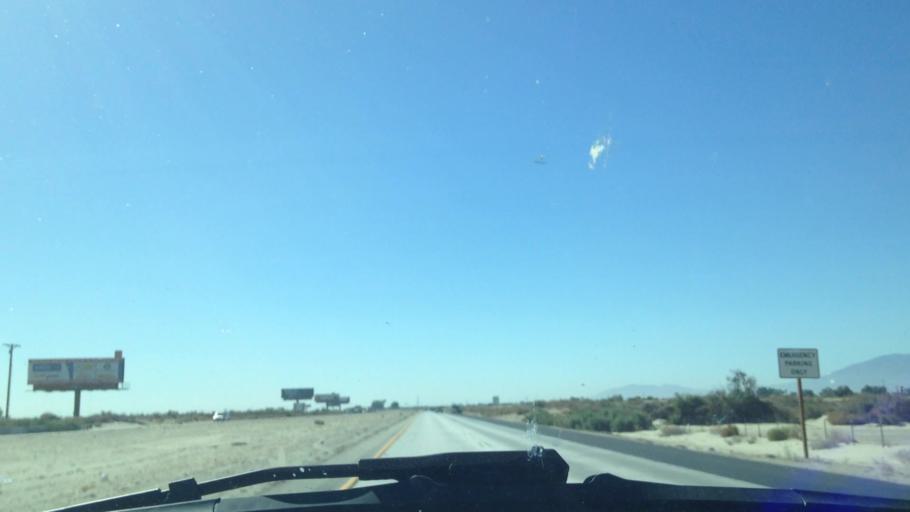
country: US
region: California
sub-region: Riverside County
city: Coachella
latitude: 33.7013
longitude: -116.1759
